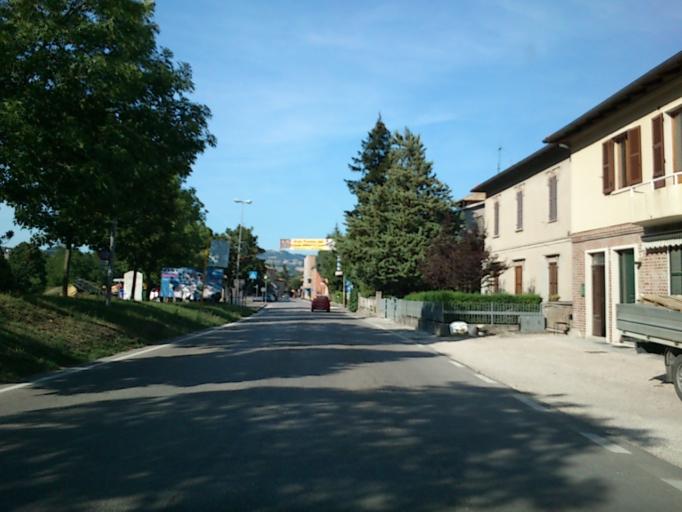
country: IT
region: The Marches
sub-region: Provincia di Pesaro e Urbino
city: Fermignano
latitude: 43.6743
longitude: 12.6437
